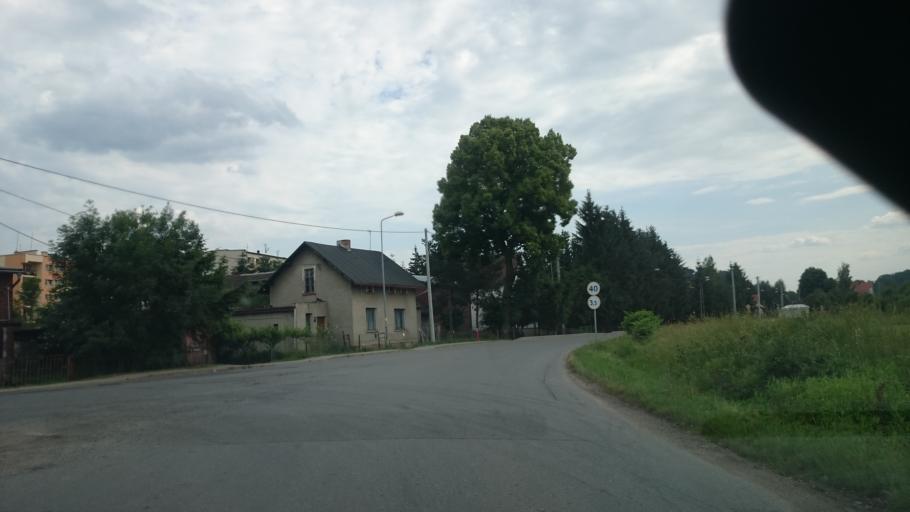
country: PL
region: Lower Silesian Voivodeship
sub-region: Powiat klodzki
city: Klodzko
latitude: 50.4559
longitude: 16.6641
